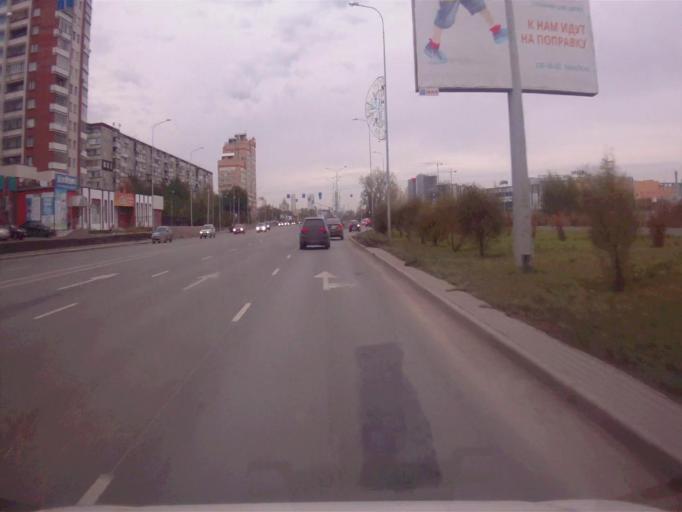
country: RU
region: Chelyabinsk
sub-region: Gorod Chelyabinsk
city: Chelyabinsk
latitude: 55.1743
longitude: 61.3452
